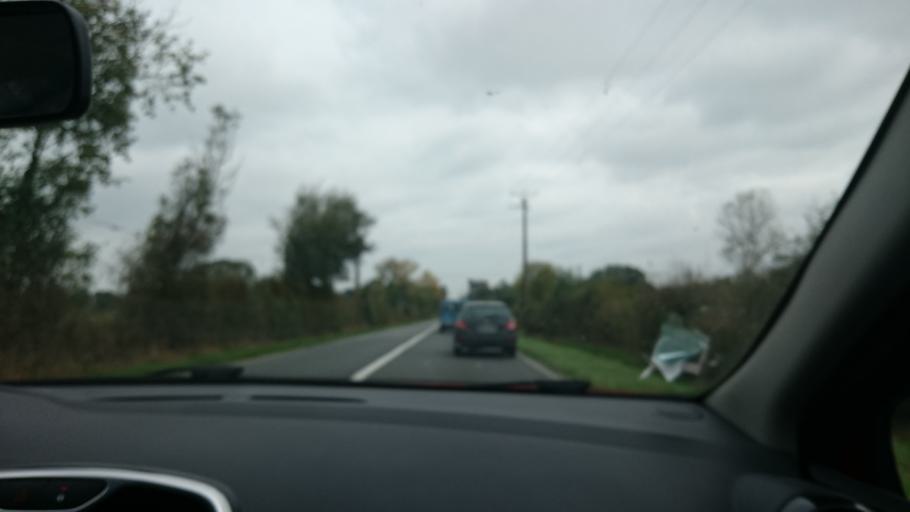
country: FR
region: Poitou-Charentes
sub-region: Departement des Deux-Sevres
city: Bressuire
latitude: 46.8418
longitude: -0.5438
